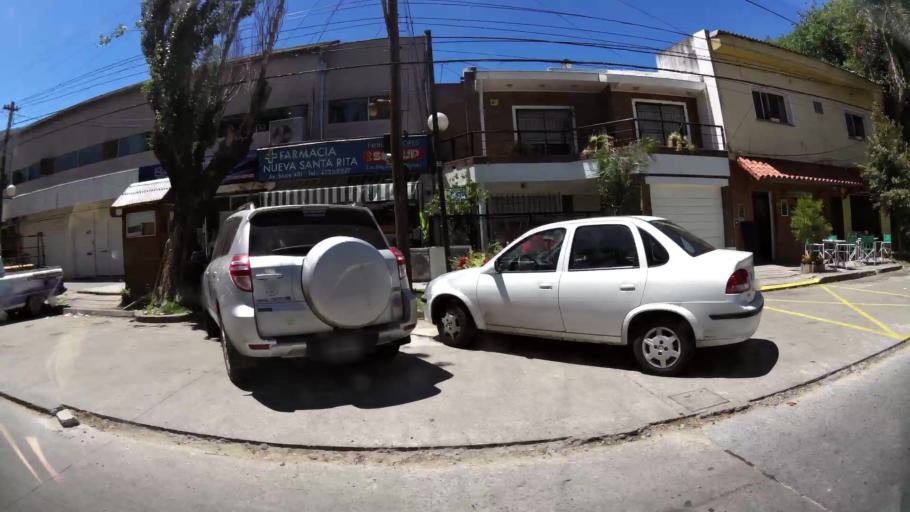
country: AR
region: Buenos Aires
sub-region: Partido de San Isidro
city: San Isidro
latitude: -34.4973
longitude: -58.5593
